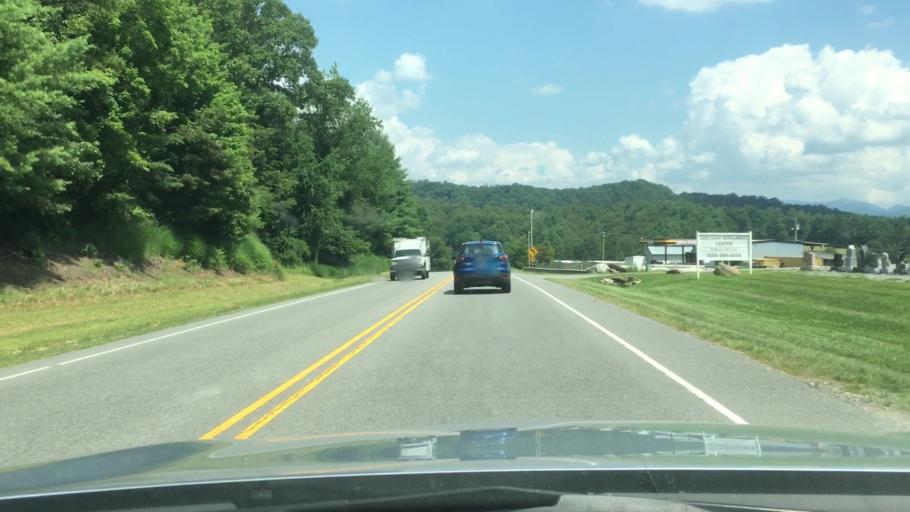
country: US
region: North Carolina
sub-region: Madison County
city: Mars Hill
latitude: 35.8252
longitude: -82.5681
